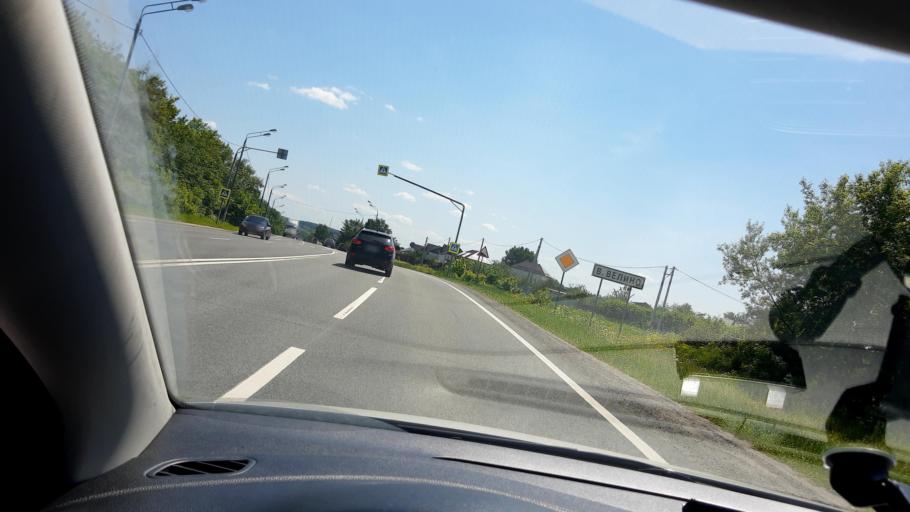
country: RU
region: Moskovskaya
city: Bronnitsy
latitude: 55.4467
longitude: 38.2090
